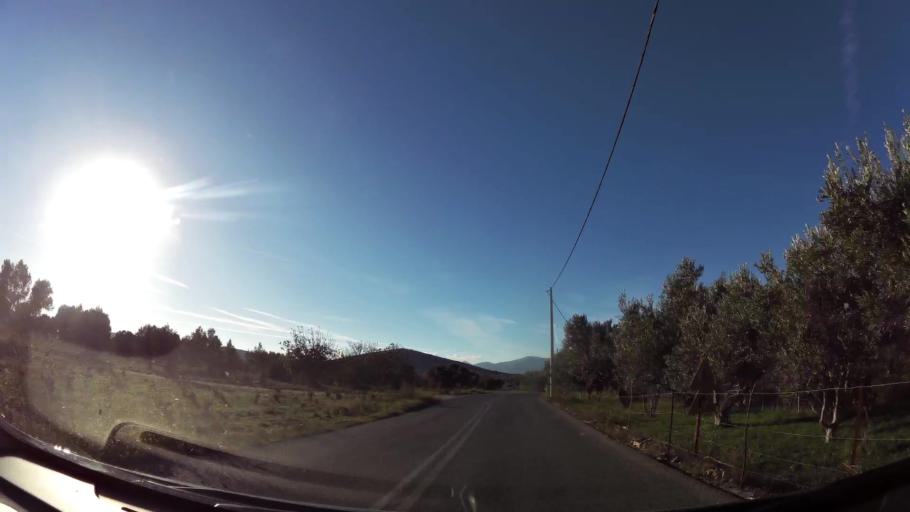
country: GR
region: Attica
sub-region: Nomarchia Anatolikis Attikis
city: Kalyvia Thorikou
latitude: 37.8464
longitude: 23.9186
